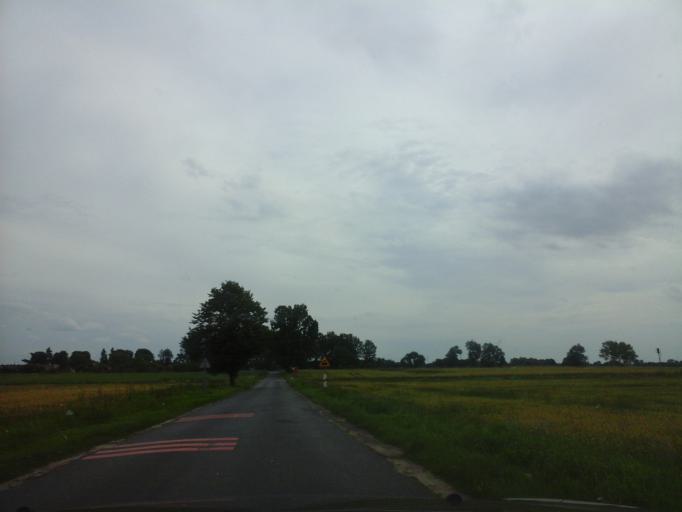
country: PL
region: West Pomeranian Voivodeship
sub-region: Powiat stargardzki
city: Stara Dabrowa
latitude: 53.3540
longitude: 15.1317
